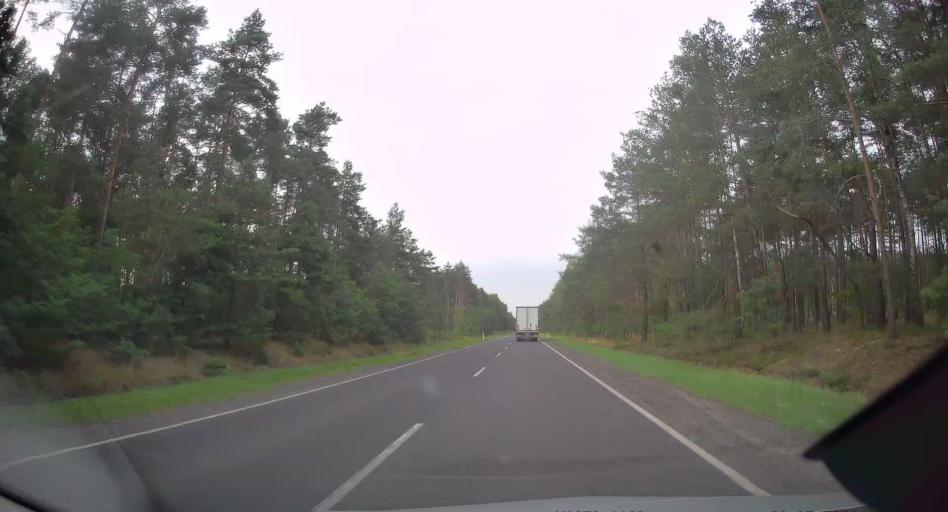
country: PL
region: Lodz Voivodeship
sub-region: Powiat radomszczanski
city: Plawno
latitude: 51.0018
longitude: 19.4181
